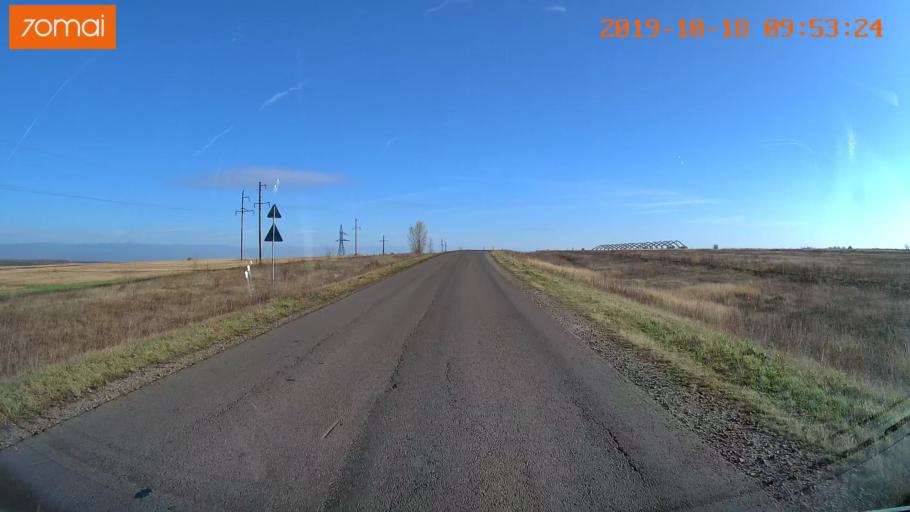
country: RU
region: Tula
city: Kazachka
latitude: 53.3605
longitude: 38.3279
